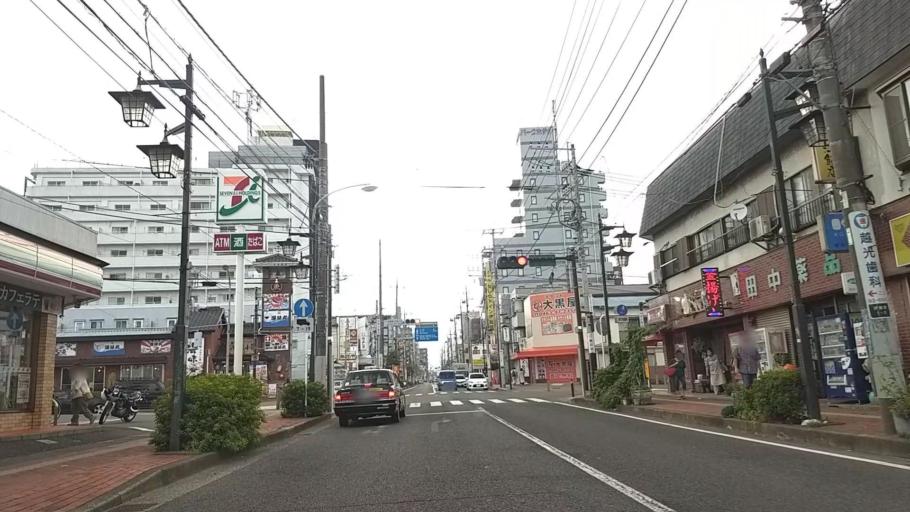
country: JP
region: Kanagawa
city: Isehara
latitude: 35.3967
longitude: 139.3112
